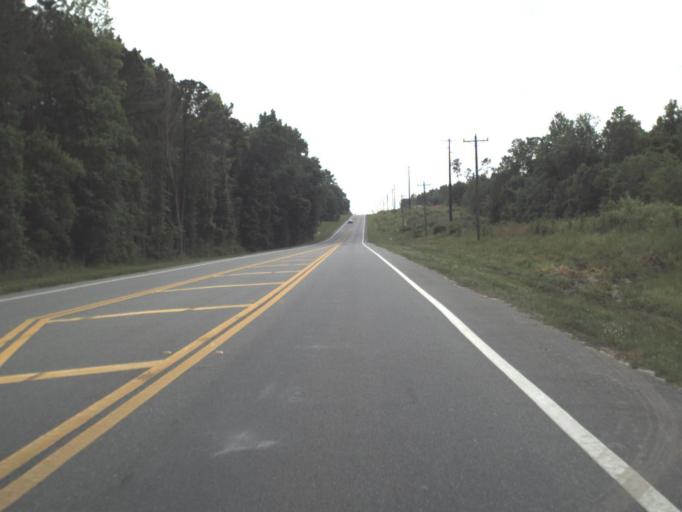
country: US
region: Florida
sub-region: Clay County
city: Middleburg
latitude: 30.0247
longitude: -81.8977
